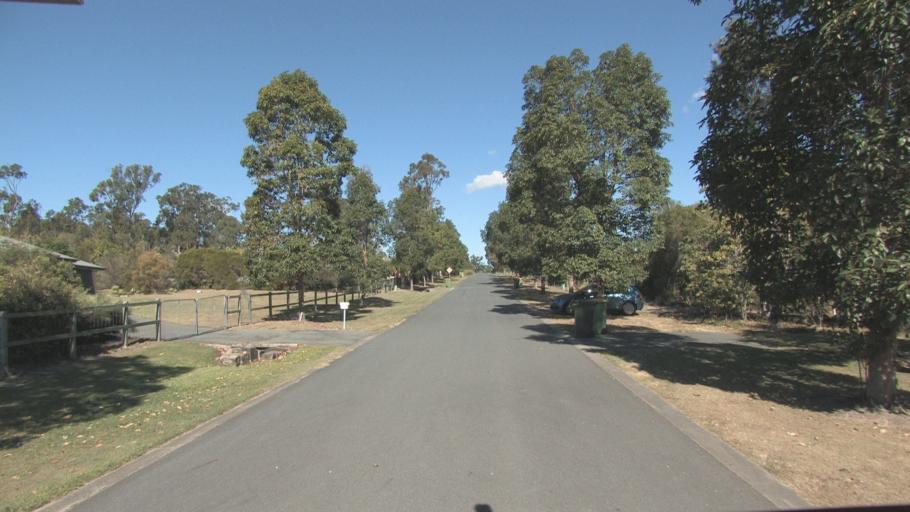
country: AU
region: Queensland
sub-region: Logan
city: North Maclean
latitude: -27.7587
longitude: 152.9522
